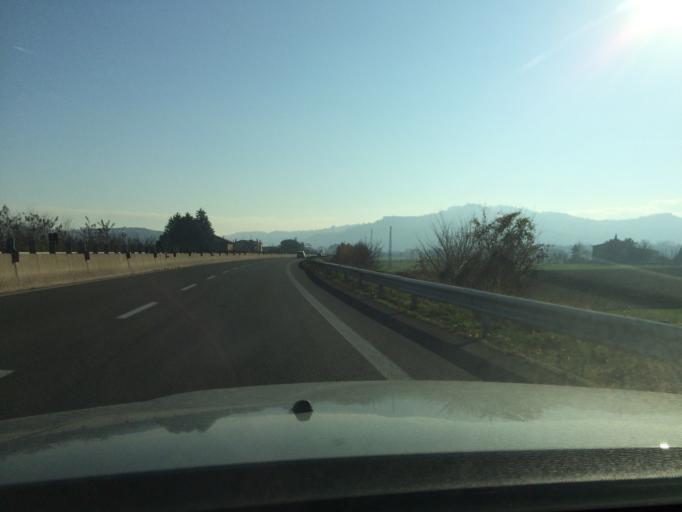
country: IT
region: Umbria
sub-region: Provincia di Perugia
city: Ponterio-Pian di Porto
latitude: 42.8135
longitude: 12.4049
